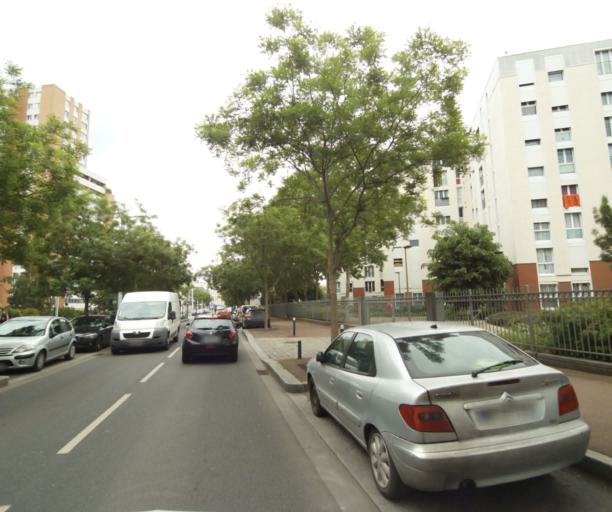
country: FR
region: Ile-de-France
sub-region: Departement des Hauts-de-Seine
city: Gennevilliers
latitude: 48.9325
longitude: 2.2918
